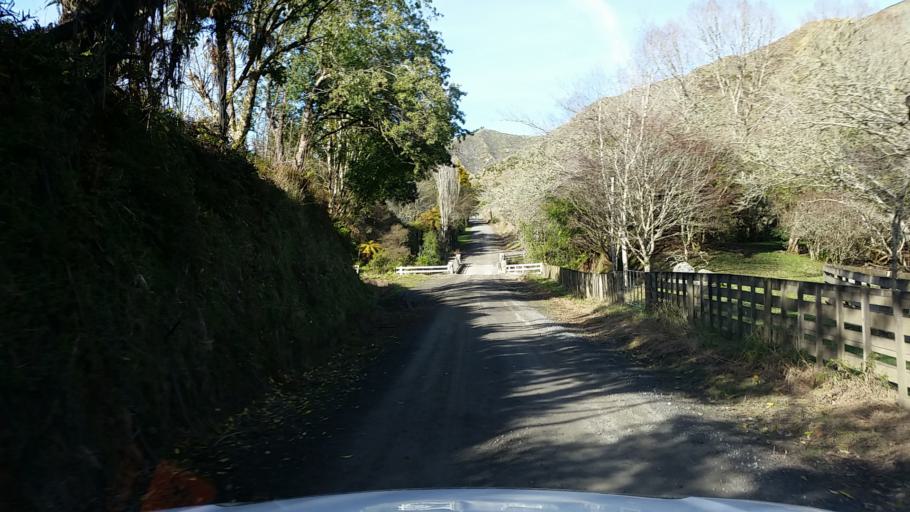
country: NZ
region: Taranaki
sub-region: South Taranaki District
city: Eltham
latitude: -39.3584
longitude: 174.5123
